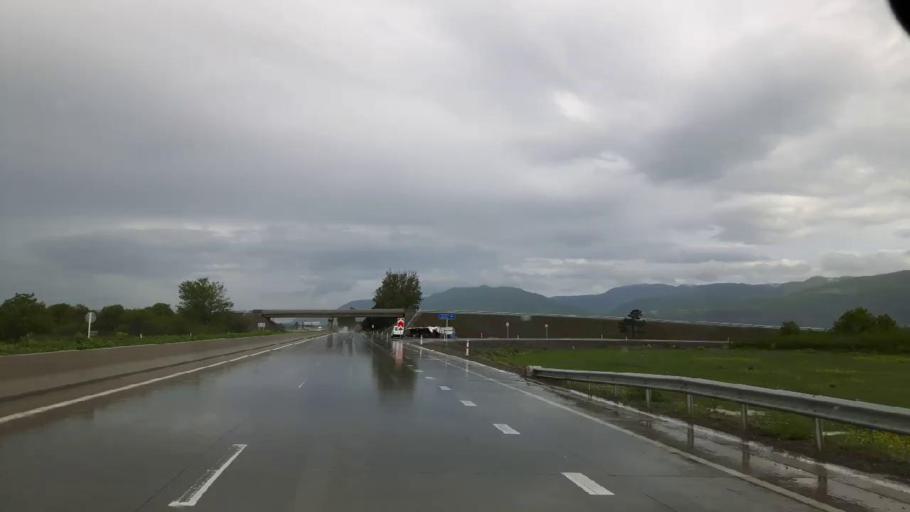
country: GE
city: Agara
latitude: 42.0324
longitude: 43.9476
